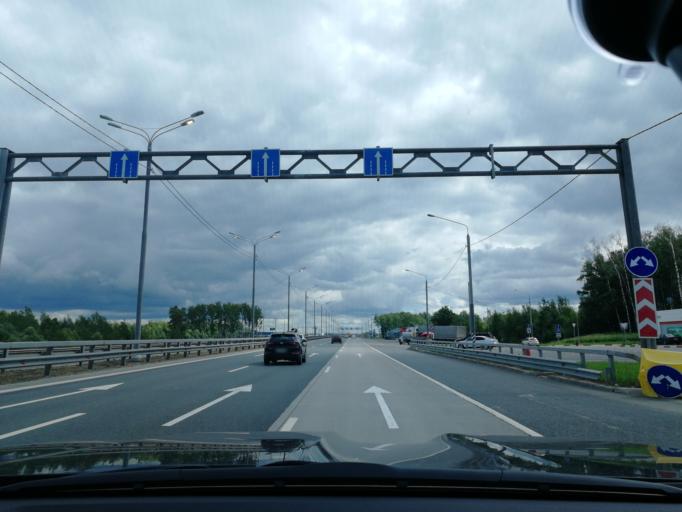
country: RU
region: Moskovskaya
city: Belyye Stolby
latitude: 55.2900
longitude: 37.8507
